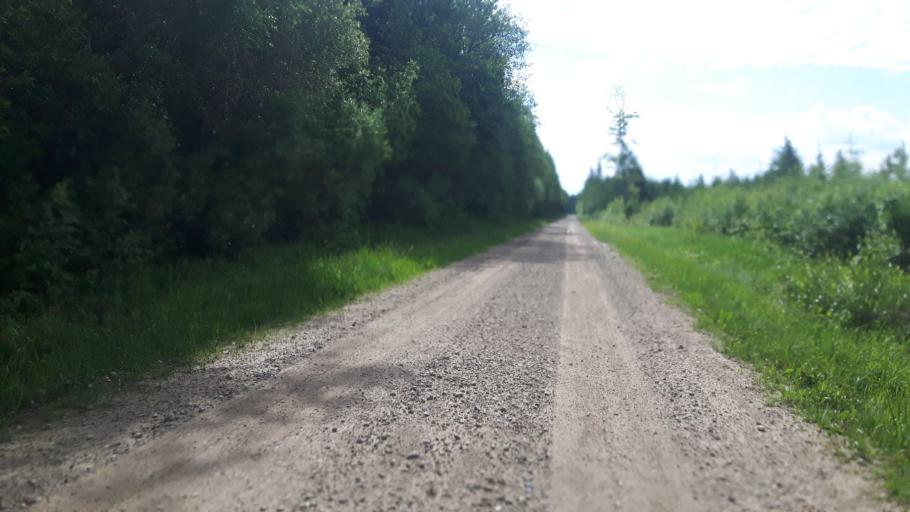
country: EE
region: Paernumaa
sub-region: Vaendra vald (alev)
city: Vandra
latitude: 58.7350
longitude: 25.0001
